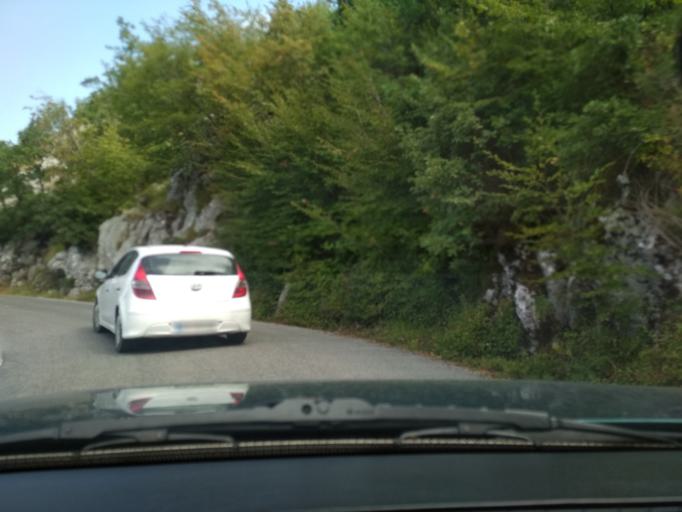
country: ME
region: Kotor
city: Kotor
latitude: 42.4107
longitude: 18.7903
